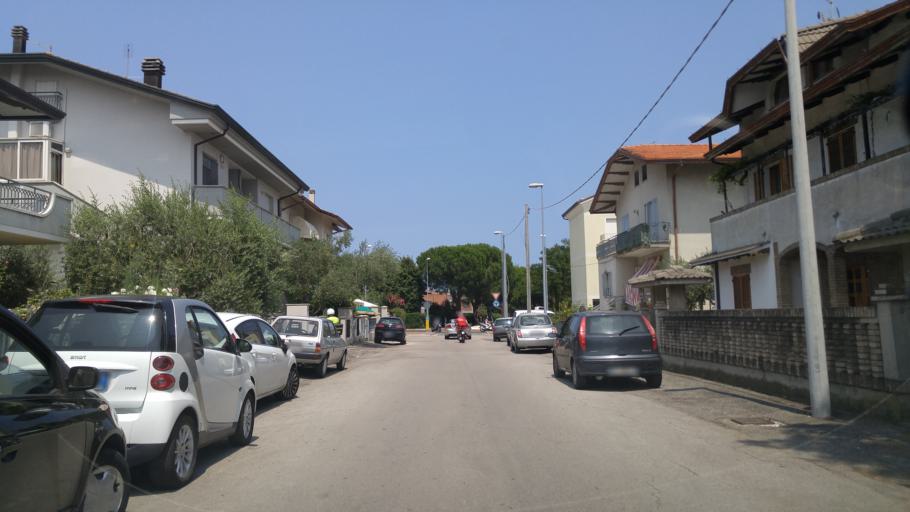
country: IT
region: Emilia-Romagna
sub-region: Provincia di Rimini
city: Cattolica
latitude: 43.9533
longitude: 12.7352
